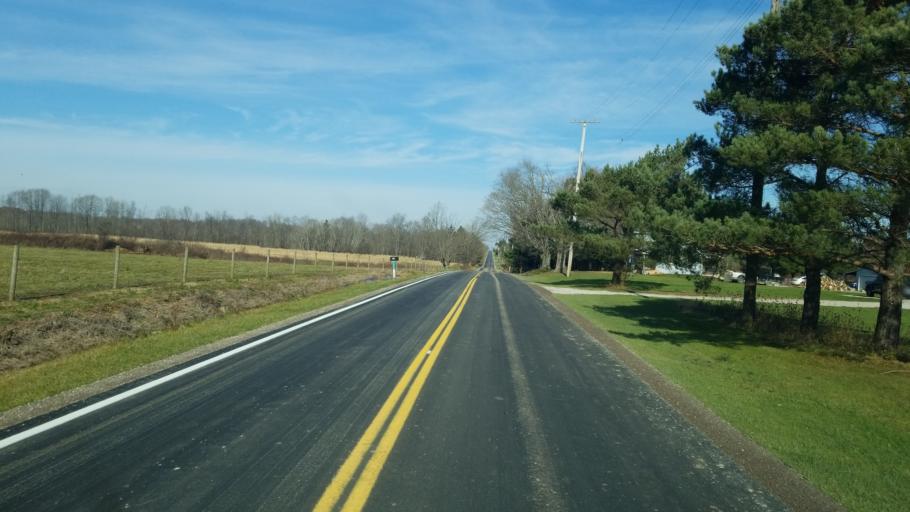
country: US
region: Ohio
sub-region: Ashtabula County
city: Geneva
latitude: 41.7115
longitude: -80.9038
